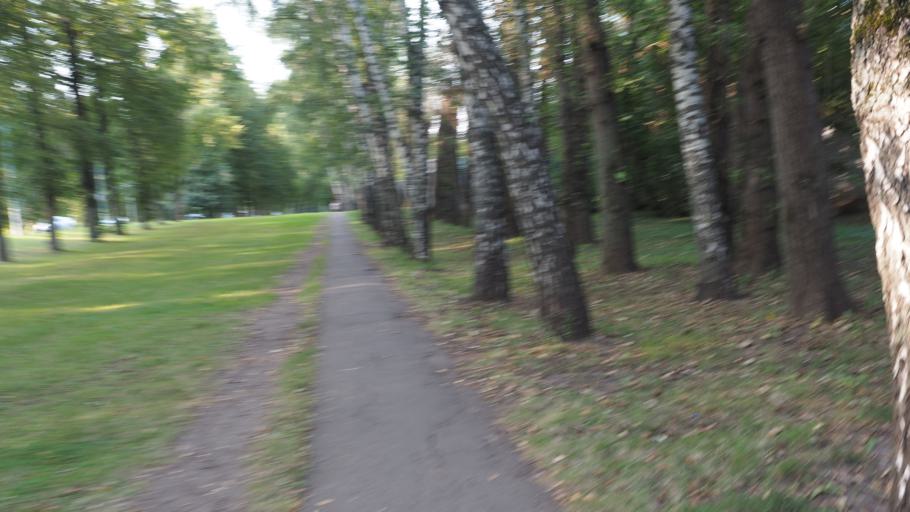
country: RU
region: Moscow
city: Orekhovo-Borisovo Severnoye
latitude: 55.6186
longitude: 37.6942
